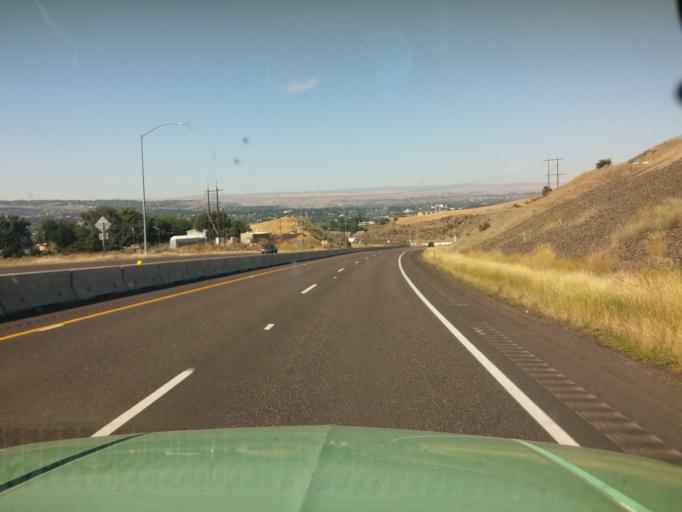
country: US
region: Idaho
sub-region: Nez Perce County
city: Lewiston
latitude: 46.4365
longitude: -116.9882
